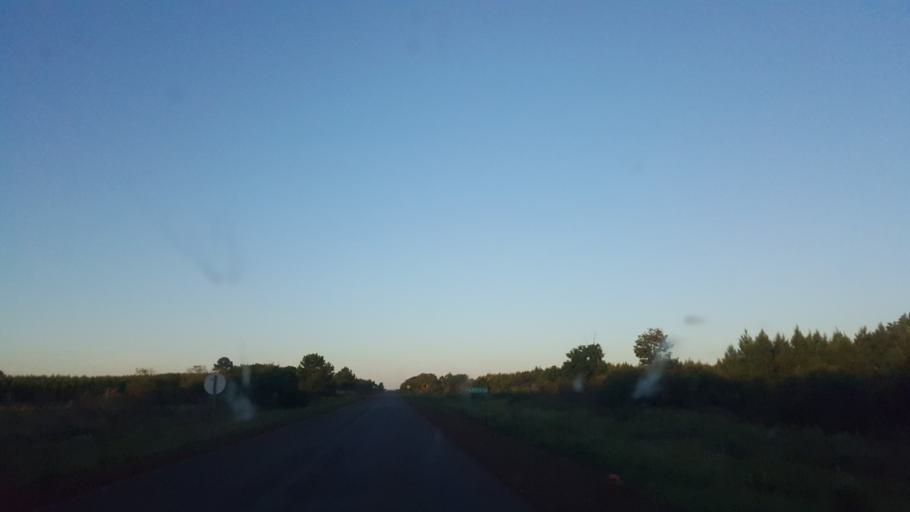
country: AR
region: Corrientes
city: Santo Tome
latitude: -28.4097
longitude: -55.9816
